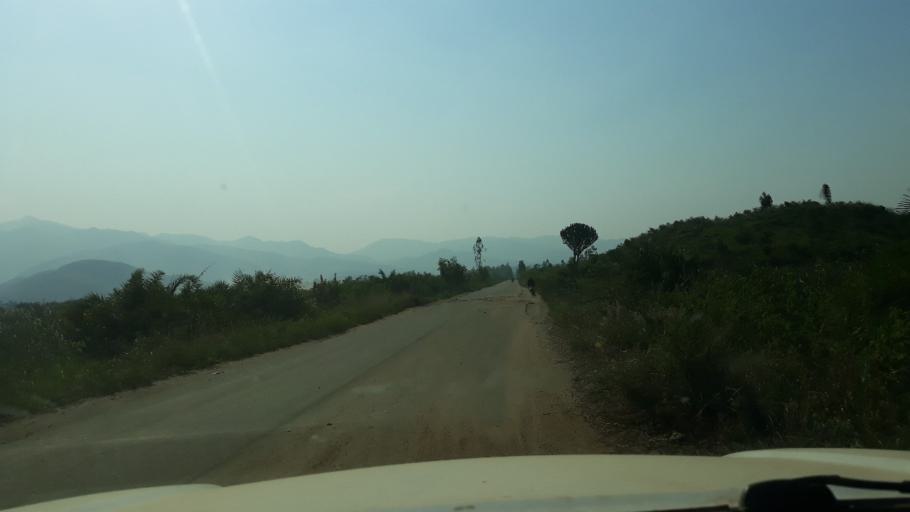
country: BI
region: Cibitoke
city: Cibitoke
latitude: -2.8241
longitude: 29.0098
